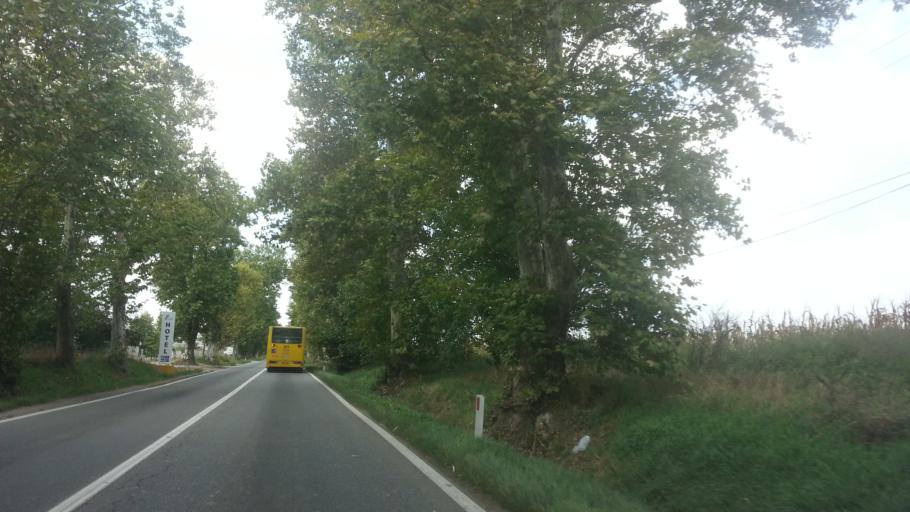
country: RS
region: Central Serbia
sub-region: Belgrade
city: Zemun
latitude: 44.8808
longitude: 20.3279
